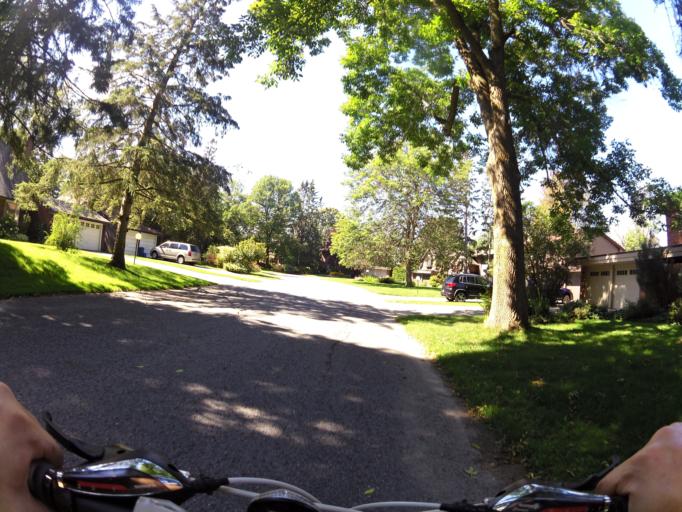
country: CA
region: Ontario
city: Bells Corners
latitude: 45.3267
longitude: -75.9080
